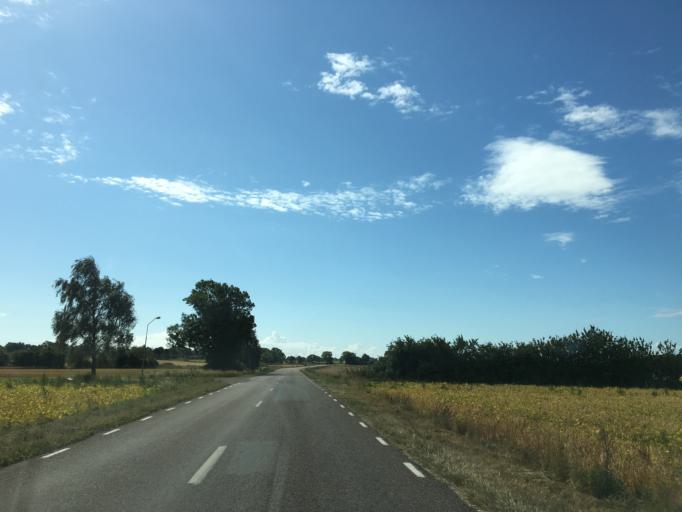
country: SE
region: Kalmar
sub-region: Morbylanga Kommun
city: Moerbylanga
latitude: 56.4119
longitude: 16.4140
